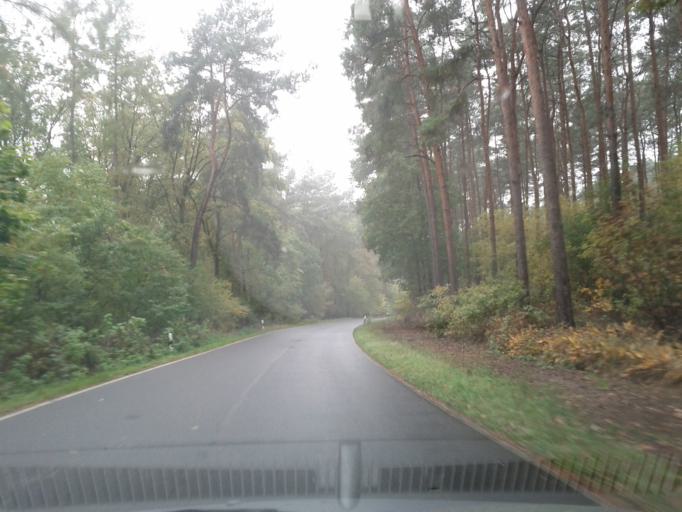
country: DE
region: Brandenburg
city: Spreenhagen
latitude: 52.3853
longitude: 13.8811
